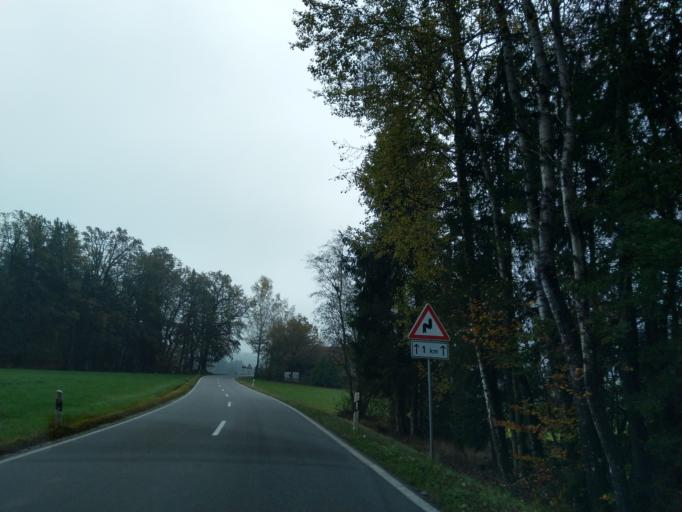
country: DE
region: Bavaria
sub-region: Lower Bavaria
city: Schollnach
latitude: 48.7802
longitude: 13.1696
